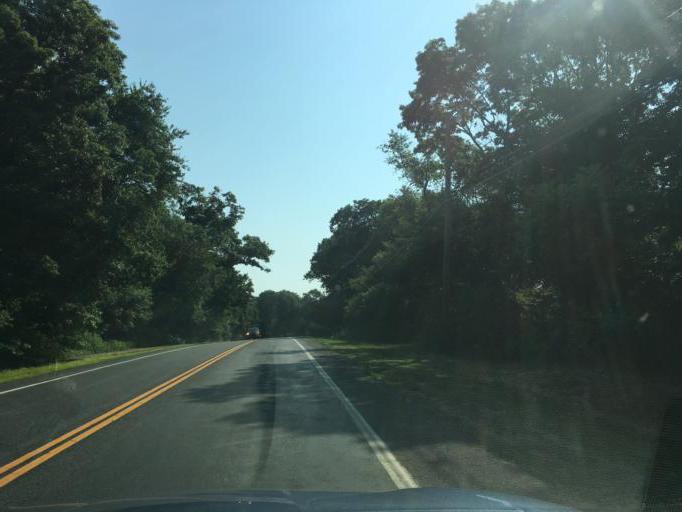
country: US
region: Rhode Island
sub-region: Washington County
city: Kingston
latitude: 41.4842
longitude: -71.4983
